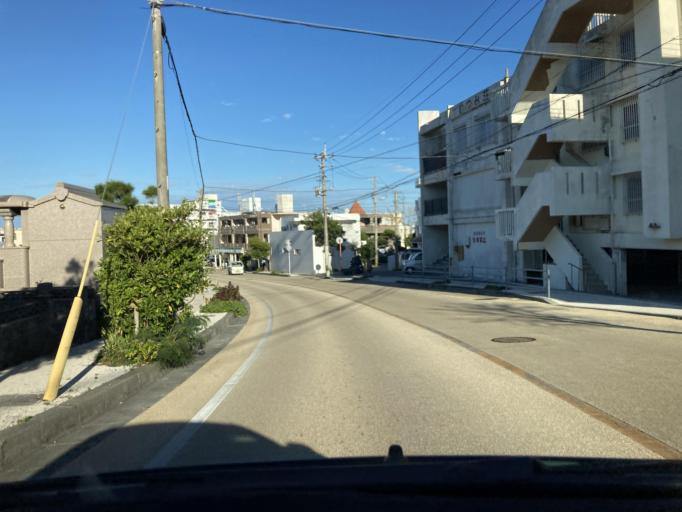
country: JP
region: Okinawa
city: Naha-shi
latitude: 26.2087
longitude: 127.7154
